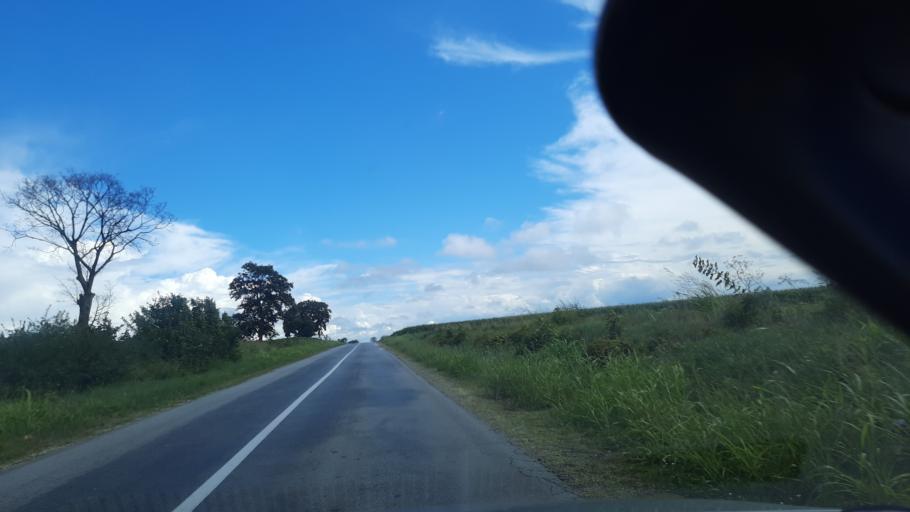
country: RS
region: Autonomna Pokrajina Vojvodina
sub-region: Sremski Okrug
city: Sremska Mitrovica
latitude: 45.0937
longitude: 19.5733
